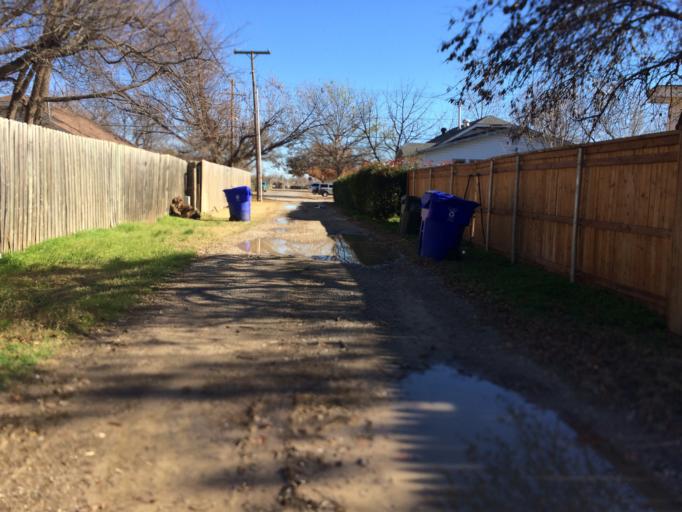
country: US
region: Oklahoma
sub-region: Cleveland County
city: Norman
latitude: 35.2236
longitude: -97.4508
